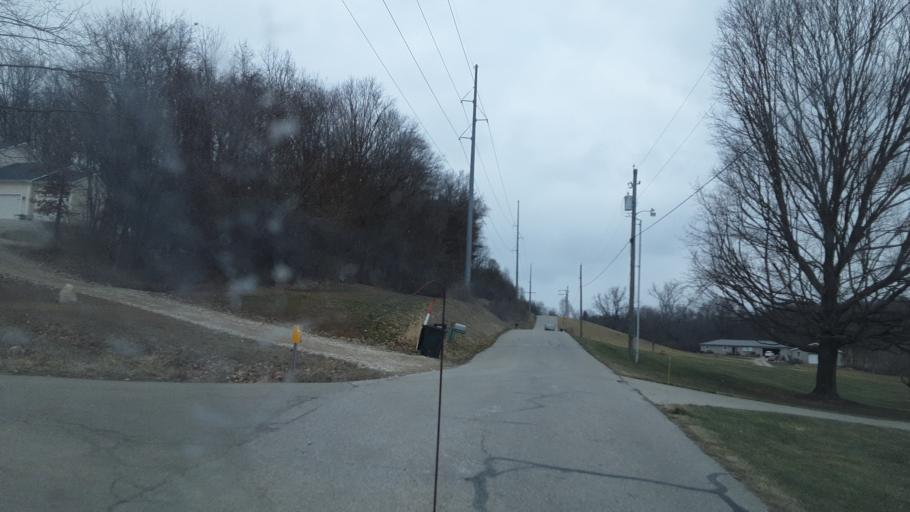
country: US
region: Ohio
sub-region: Perry County
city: Thornport
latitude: 39.9360
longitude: -82.3956
